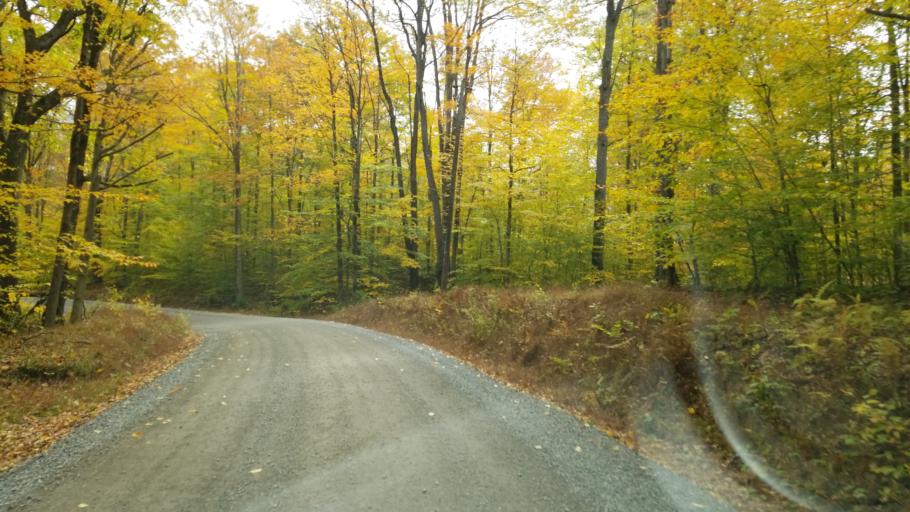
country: US
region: Pennsylvania
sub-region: Clearfield County
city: Clearfield
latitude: 41.1932
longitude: -78.3853
